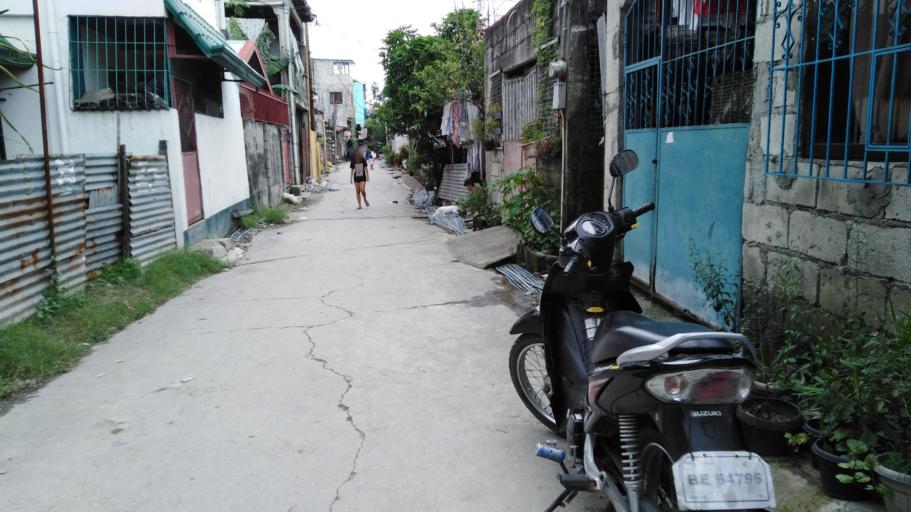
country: PH
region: Calabarzon
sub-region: Province of Rizal
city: Taytay
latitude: 14.5454
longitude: 121.1203
